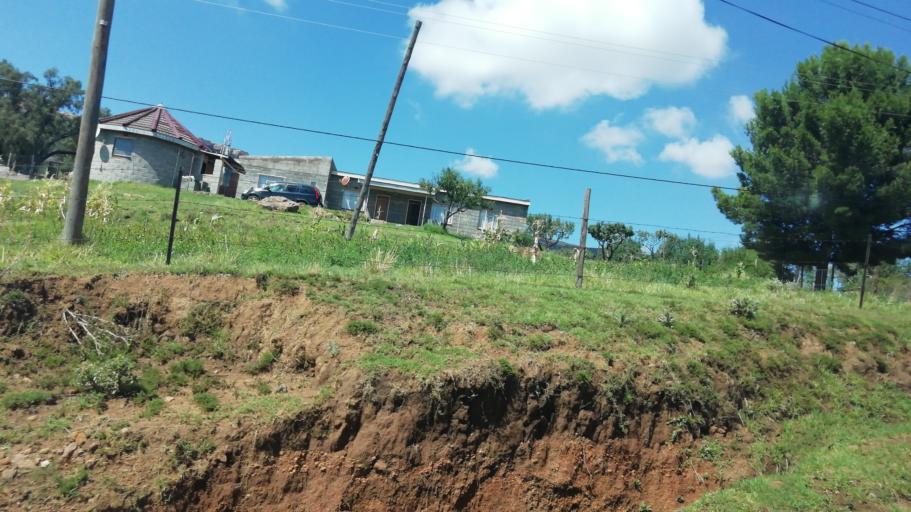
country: LS
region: Maseru
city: Nako
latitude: -29.6243
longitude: 27.5151
